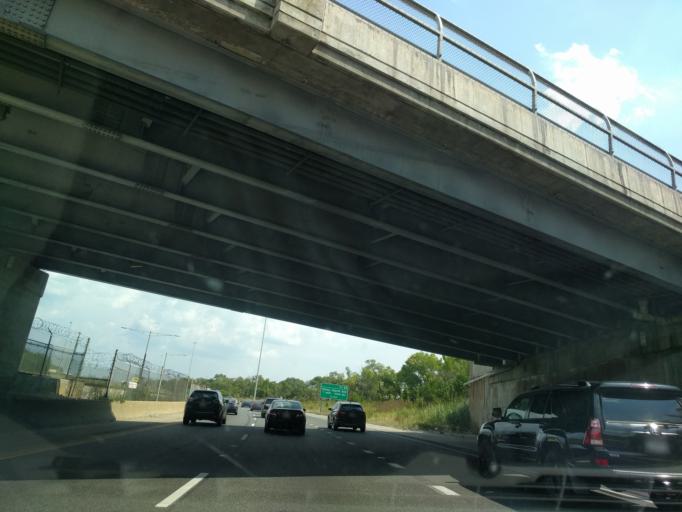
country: US
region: Illinois
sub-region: Cook County
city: Calumet Park
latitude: 41.7135
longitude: -87.6205
